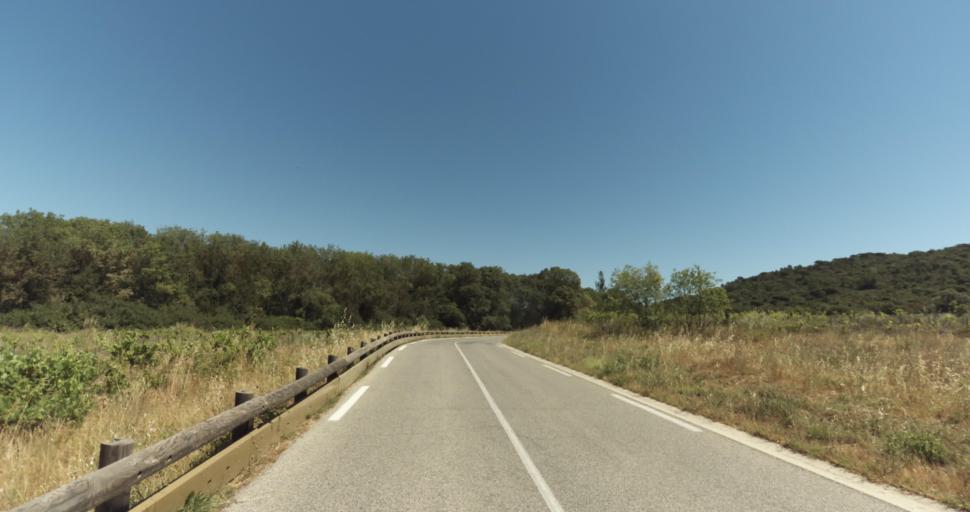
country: FR
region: Provence-Alpes-Cote d'Azur
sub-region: Departement du Var
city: Gassin
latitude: 43.2447
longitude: 6.5755
